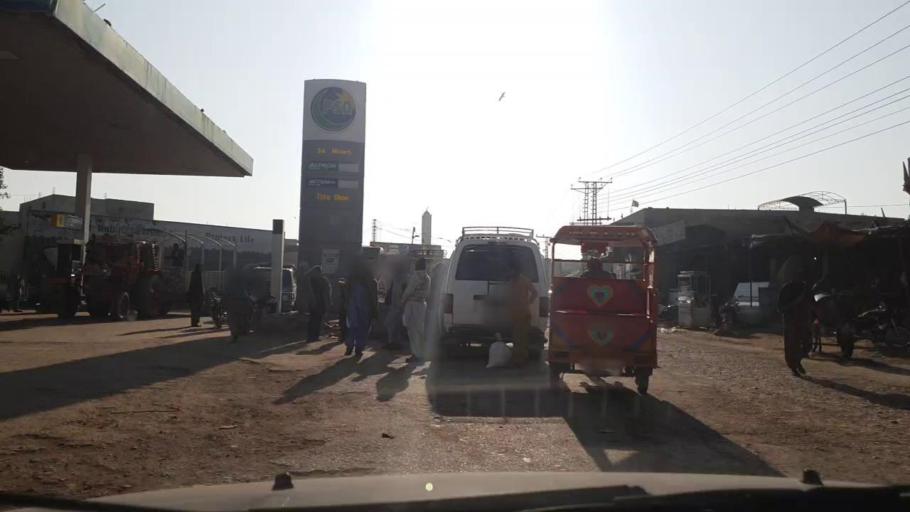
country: PK
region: Sindh
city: Tando Bago
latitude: 24.7864
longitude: 68.9657
